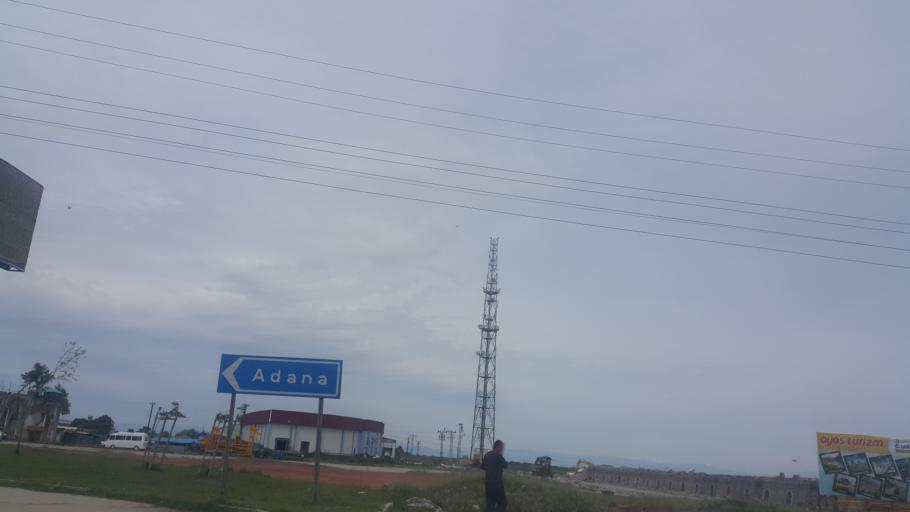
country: TR
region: Adana
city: Ceyhan
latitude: 37.0521
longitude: 35.8103
